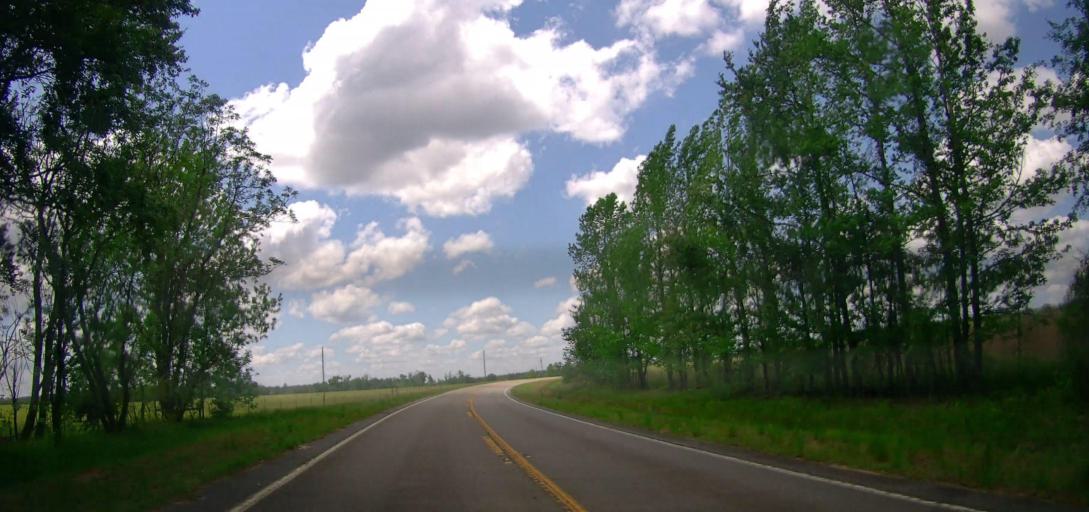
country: US
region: Georgia
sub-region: Dodge County
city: Chester
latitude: 32.5476
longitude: -83.1784
